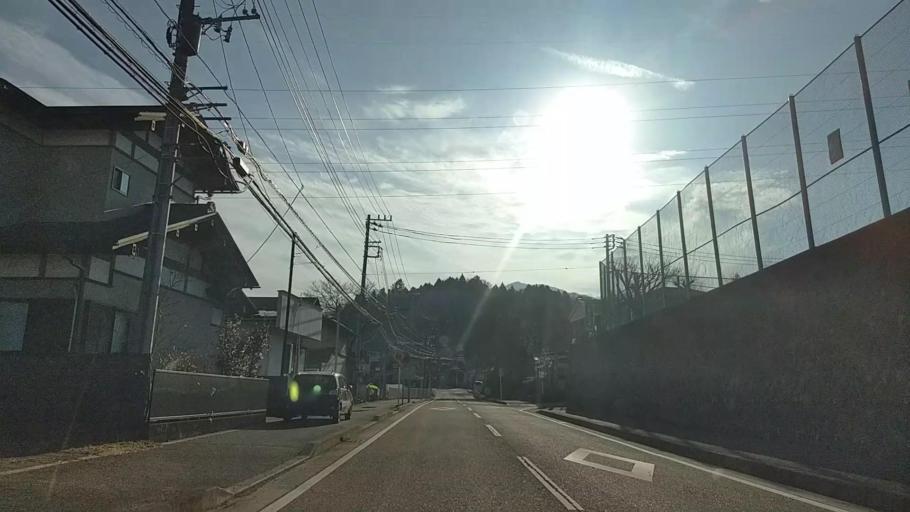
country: JP
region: Yamanashi
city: Uenohara
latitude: 35.5453
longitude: 139.2181
